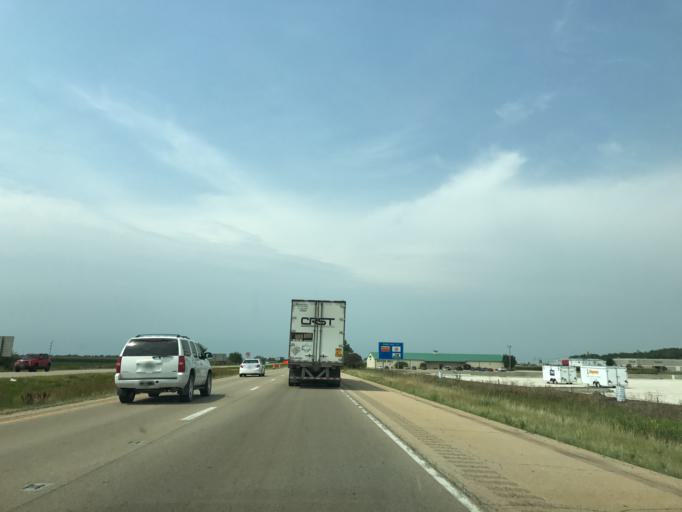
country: US
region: Illinois
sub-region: LaSalle County
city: Peru
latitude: 41.3651
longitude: -89.1368
